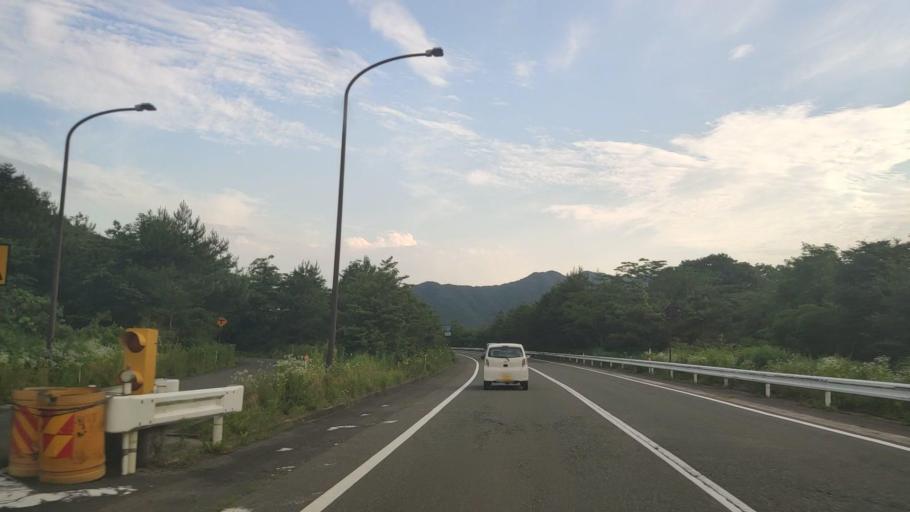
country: JP
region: Tottori
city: Kurayoshi
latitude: 35.2987
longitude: 133.7368
